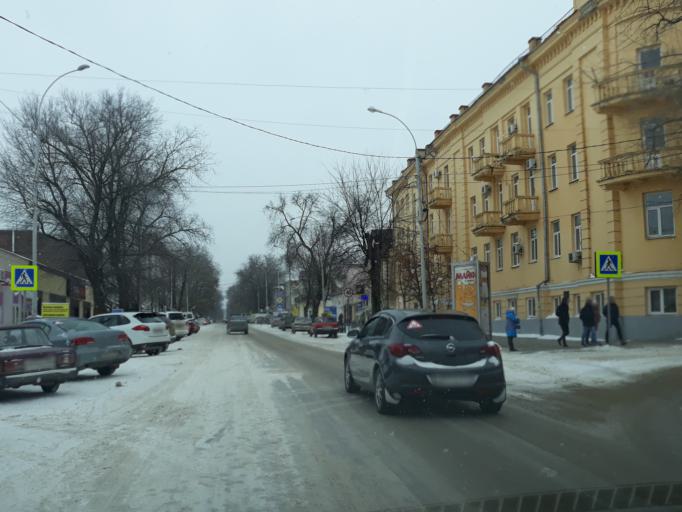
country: RU
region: Rostov
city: Taganrog
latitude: 47.2155
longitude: 38.9290
